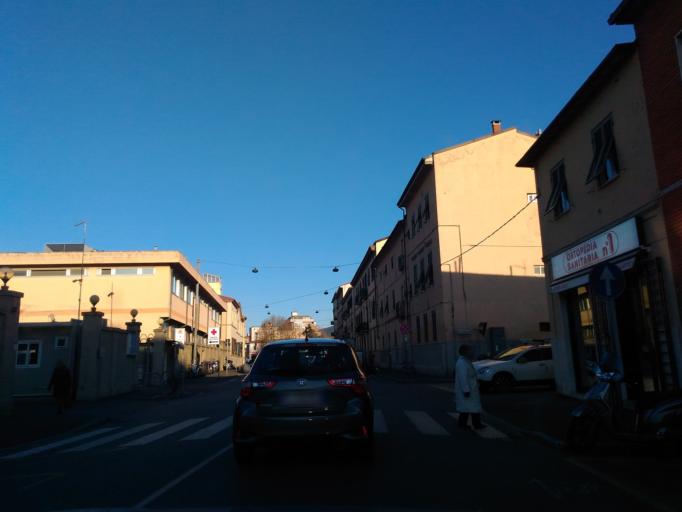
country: IT
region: Tuscany
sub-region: Provincia di Livorno
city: Livorno
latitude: 43.5488
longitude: 10.3254
